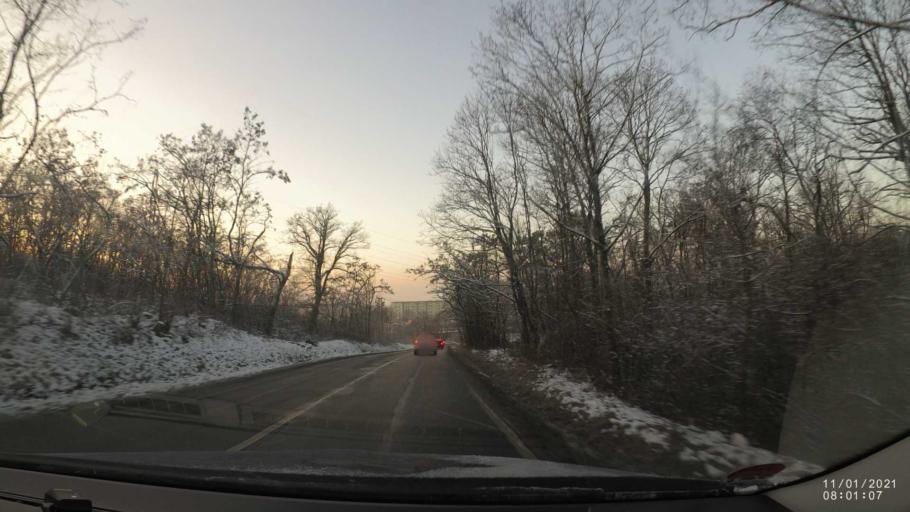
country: CZ
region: South Moravian
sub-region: Mesto Brno
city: Mokra Hora
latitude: 49.2394
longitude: 16.6274
